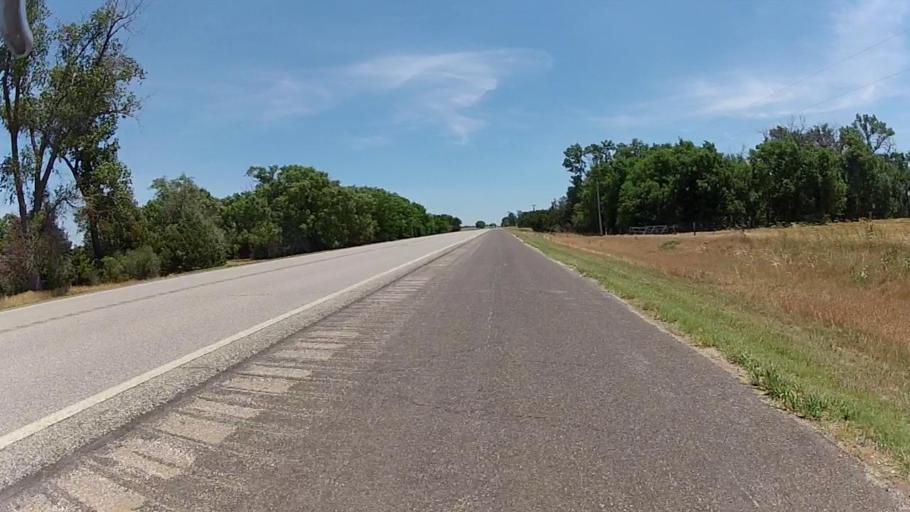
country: US
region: Kansas
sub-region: Barber County
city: Medicine Lodge
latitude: 37.2536
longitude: -98.4056
